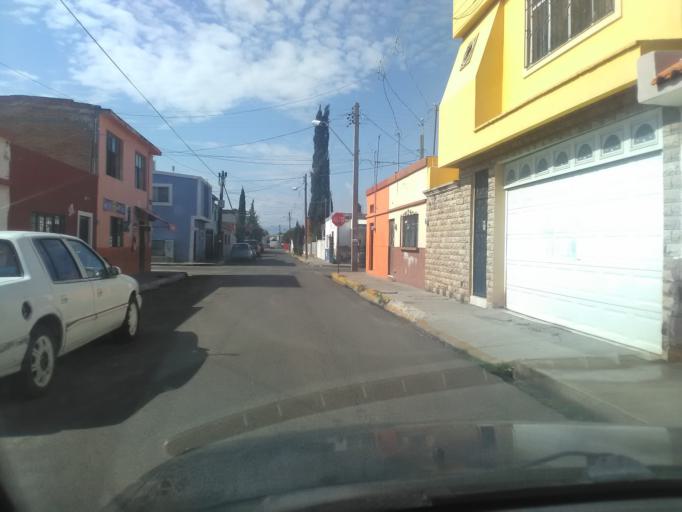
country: MX
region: Durango
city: Victoria de Durango
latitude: 24.0224
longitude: -104.6577
